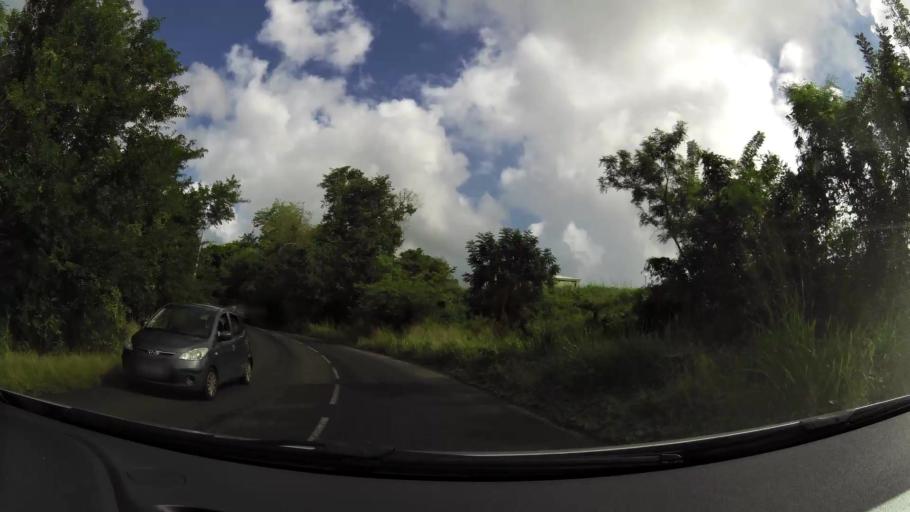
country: MQ
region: Martinique
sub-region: Martinique
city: Sainte-Luce
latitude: 14.4962
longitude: -60.9832
